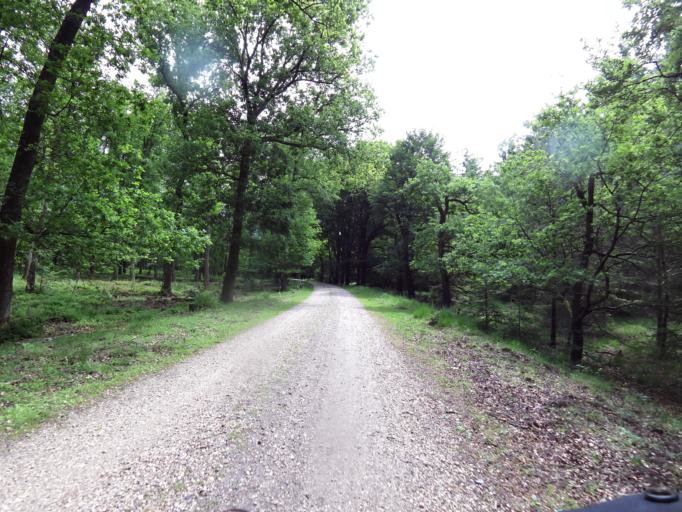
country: NL
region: Gelderland
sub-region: Gemeente Apeldoorn
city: Uddel
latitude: 52.2713
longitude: 5.8157
